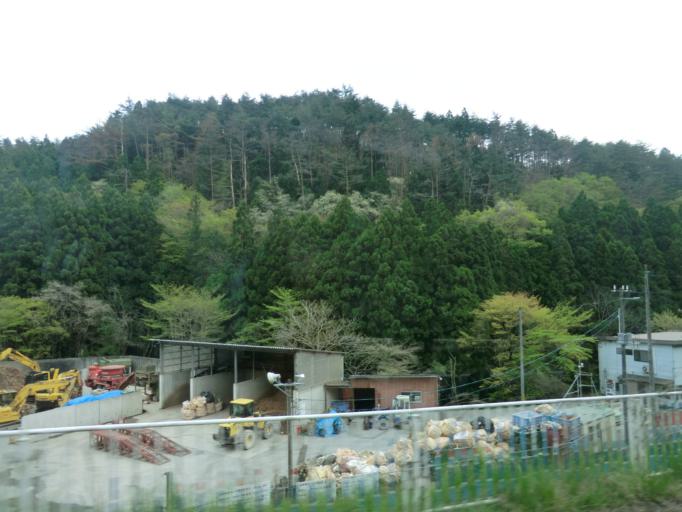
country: JP
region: Iwate
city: Ofunato
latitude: 38.9265
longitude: 141.5978
